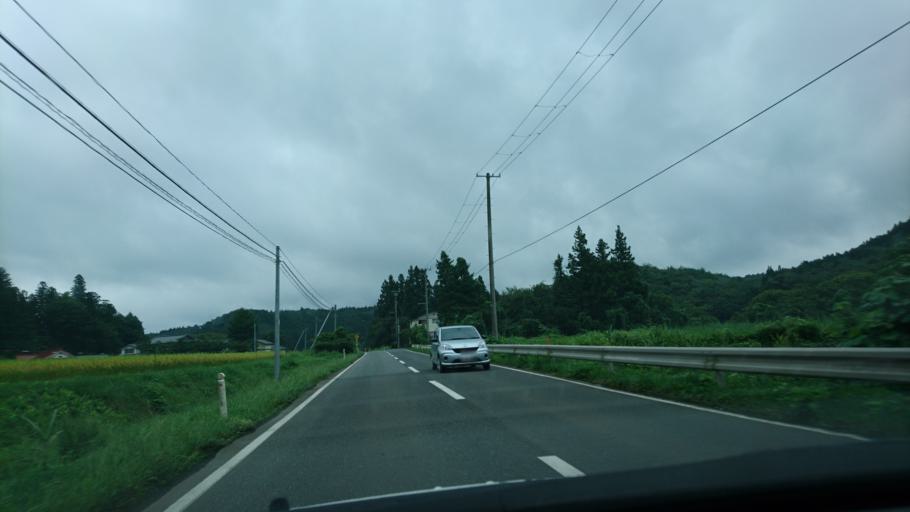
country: JP
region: Iwate
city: Ichinoseki
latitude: 38.9097
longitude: 141.0604
